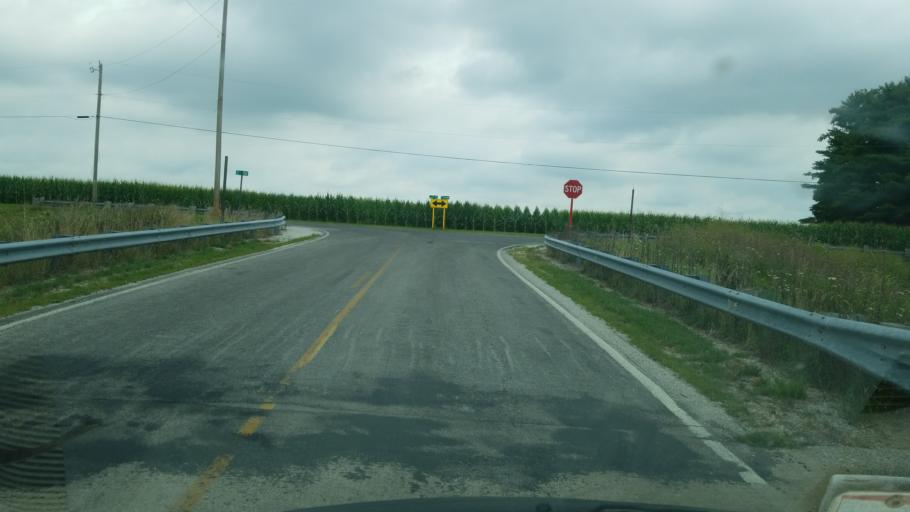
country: US
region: Ohio
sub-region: Seneca County
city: Tiffin
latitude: 41.2103
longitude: -83.1463
